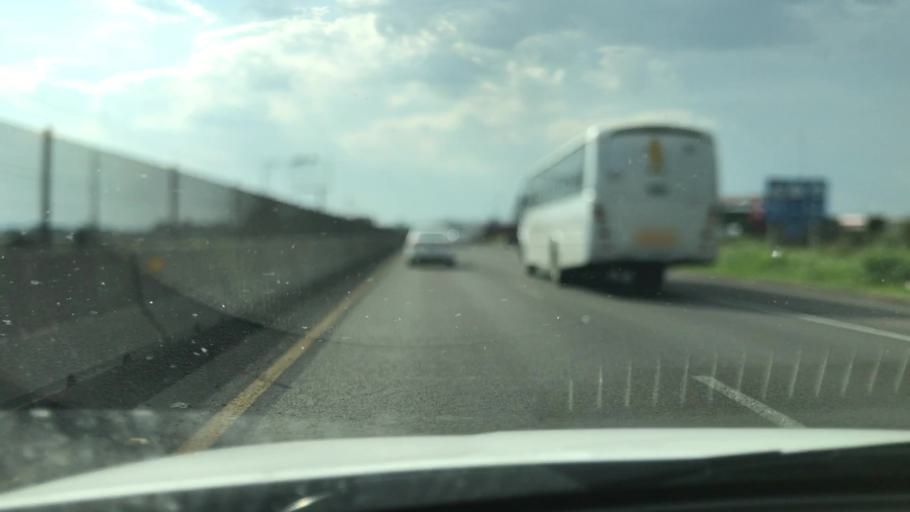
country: MX
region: Guanajuato
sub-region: Salamanca
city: San Vicente de Flores
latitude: 20.5938
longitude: -101.2339
